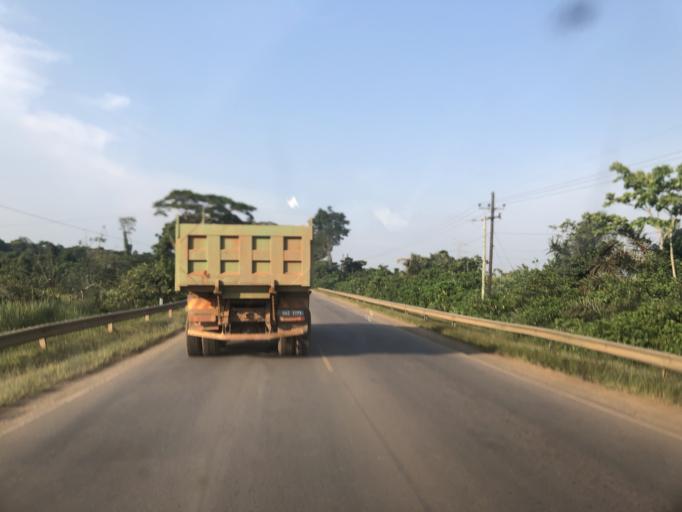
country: UG
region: Central Region
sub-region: Butambala District
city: Gombe
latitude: 0.0954
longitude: 32.1529
